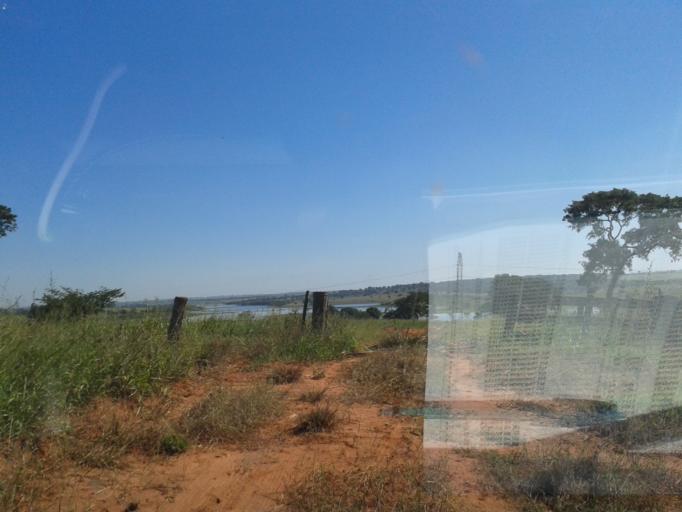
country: BR
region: Minas Gerais
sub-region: Santa Vitoria
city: Santa Vitoria
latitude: -19.0086
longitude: -50.3223
